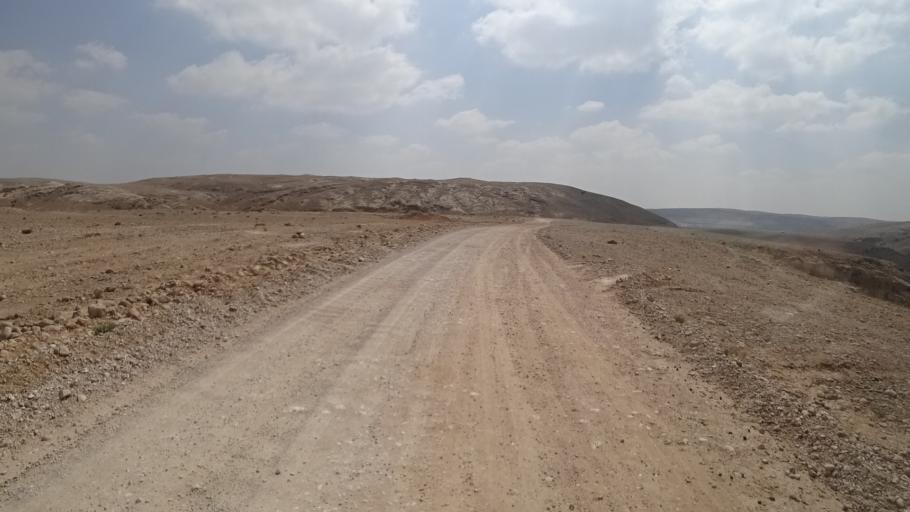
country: OM
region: Zufar
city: Salalah
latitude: 17.2379
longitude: 53.8962
